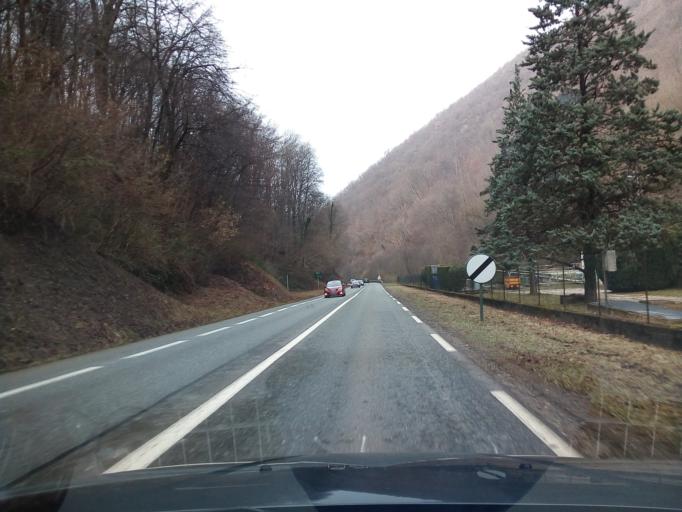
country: FR
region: Rhone-Alpes
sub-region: Departement de l'Isere
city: Gieres
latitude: 45.1635
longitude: 5.8114
